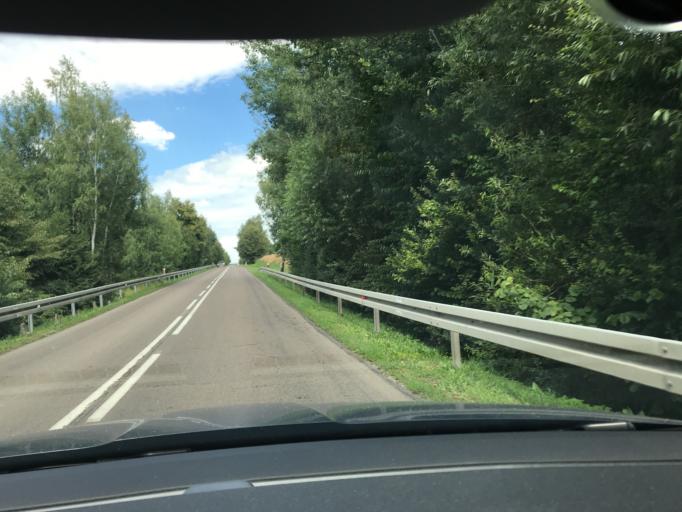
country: PL
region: Lublin Voivodeship
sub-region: Powiat zamojski
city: Szczebrzeszyn
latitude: 50.7134
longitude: 22.9392
